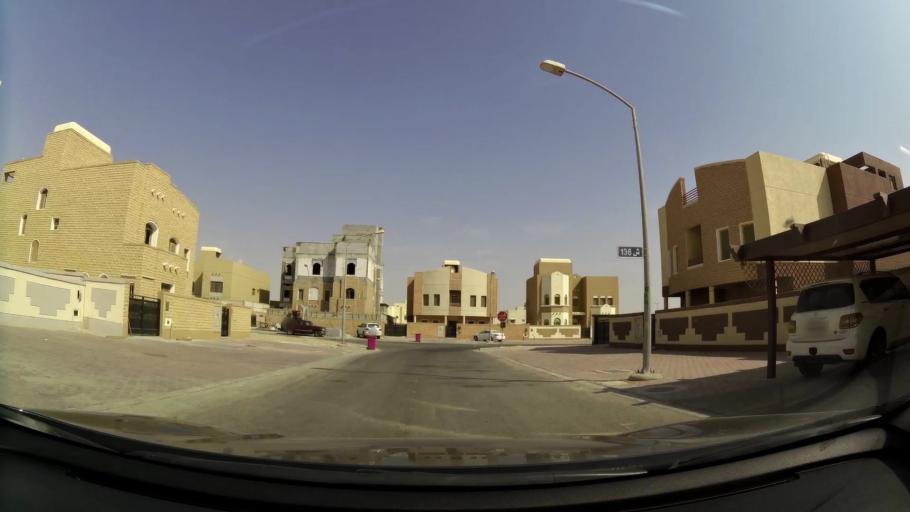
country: KW
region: Al Ahmadi
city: Al Wafrah
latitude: 28.8045
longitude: 48.0580
